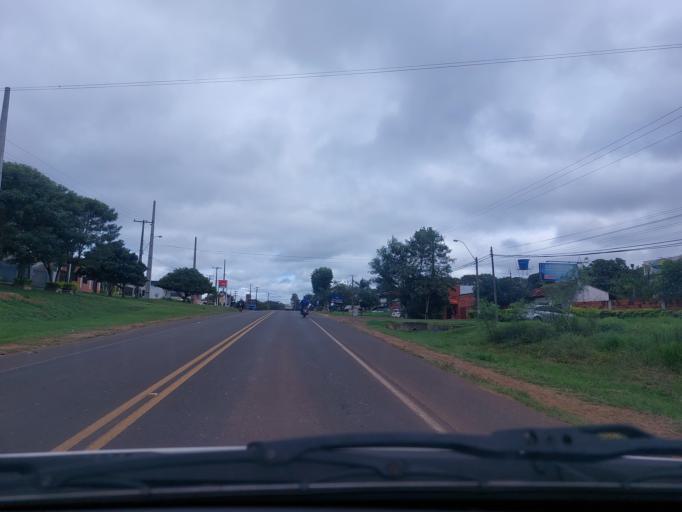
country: PY
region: San Pedro
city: Guayaybi
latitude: -24.6637
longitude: -56.4280
